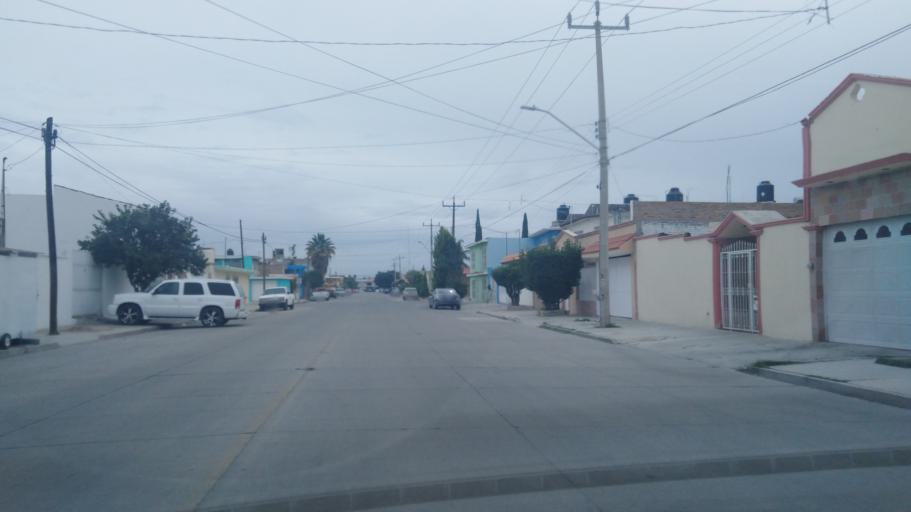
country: MX
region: Durango
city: Victoria de Durango
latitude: 24.0305
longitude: -104.6260
